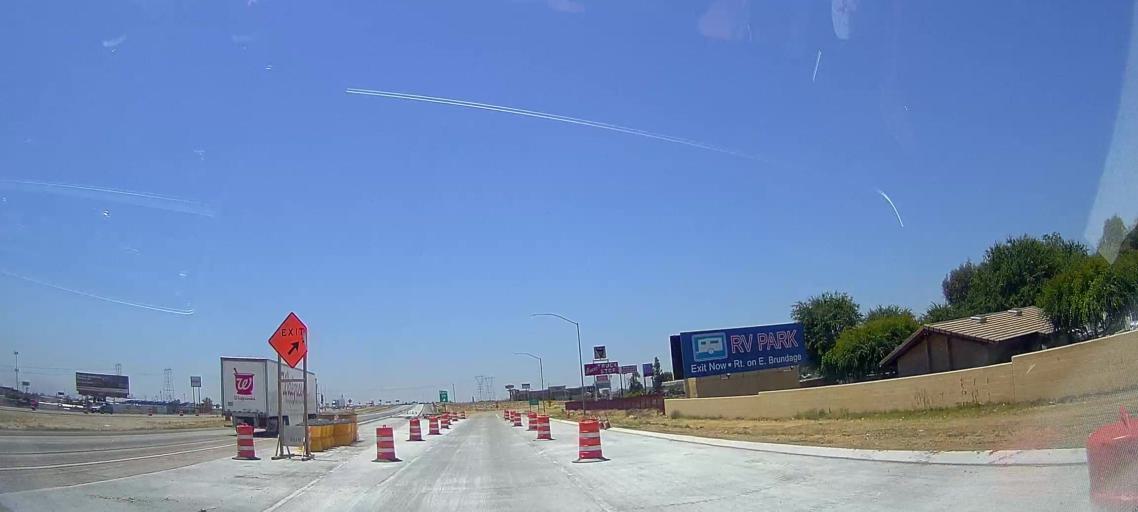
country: US
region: California
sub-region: Kern County
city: Lamont
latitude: 35.3523
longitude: -118.9093
